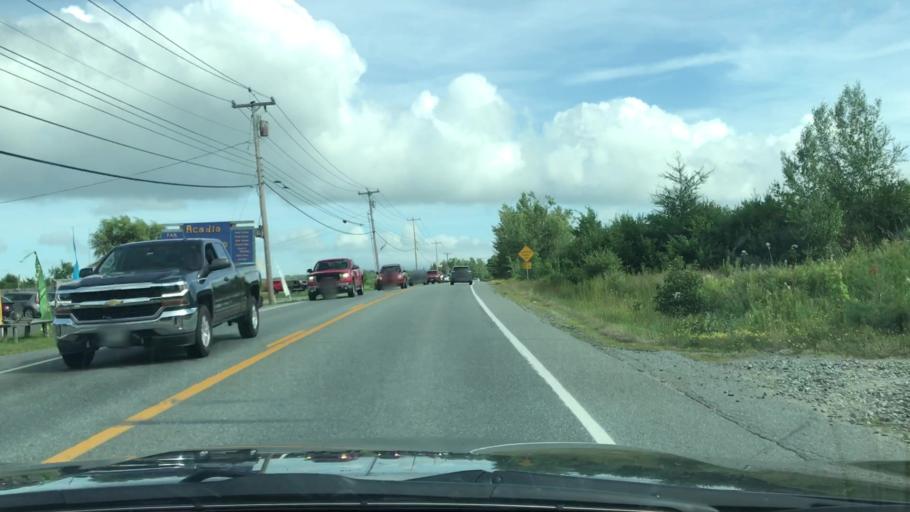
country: US
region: Maine
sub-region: Hancock County
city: Trenton
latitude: 44.4852
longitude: -68.3676
